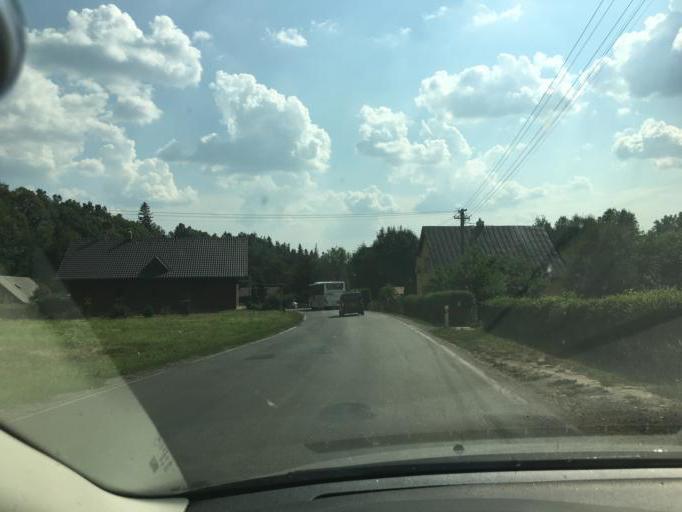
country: CZ
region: Kralovehradecky
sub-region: Okres Trutnov
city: Rudnik
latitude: 50.6215
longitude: 15.7105
